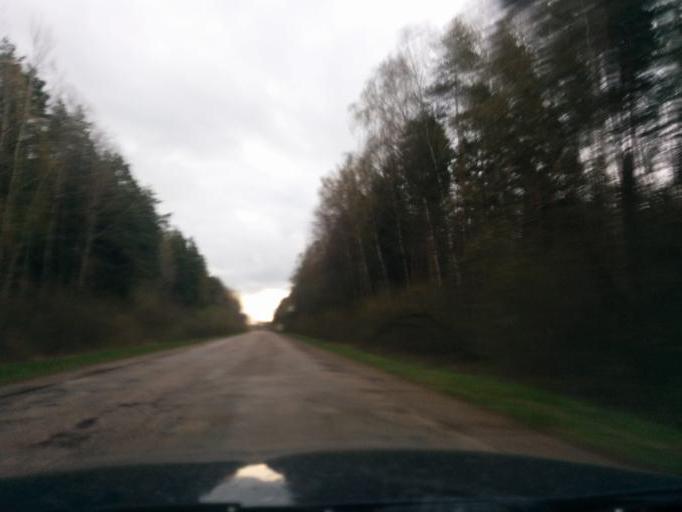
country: LT
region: Siauliu apskritis
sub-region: Joniskis
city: Joniskis
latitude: 56.4161
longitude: 23.6285
